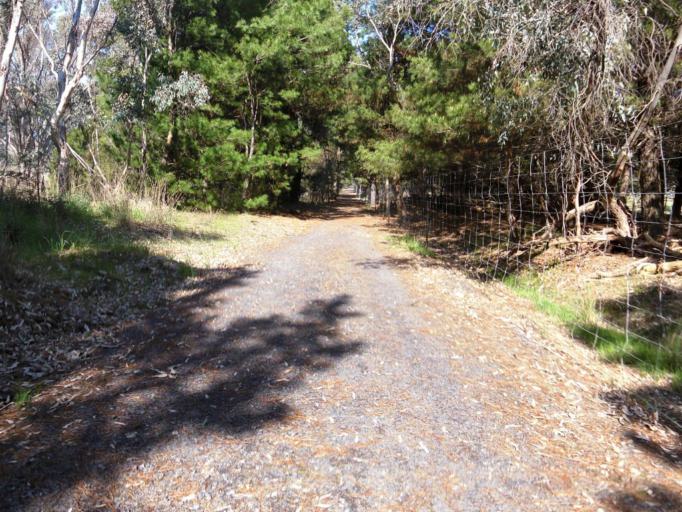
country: AU
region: Victoria
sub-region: Murrindindi
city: Alexandra
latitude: -36.9952
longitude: 145.7409
